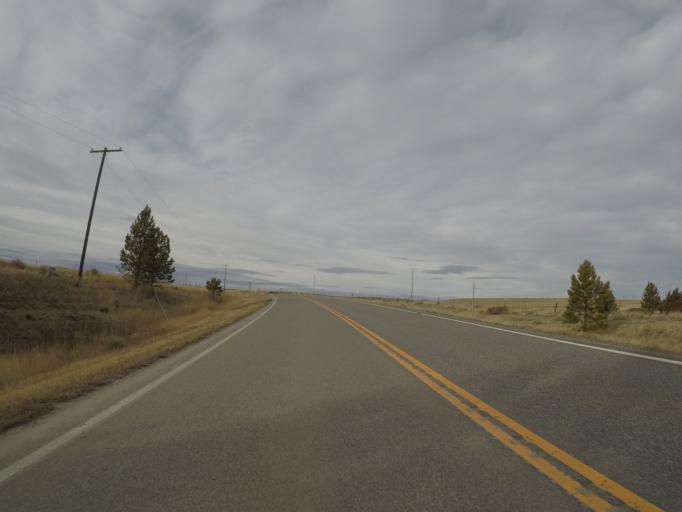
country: US
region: Montana
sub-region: Yellowstone County
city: Laurel
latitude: 45.8408
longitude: -108.7217
